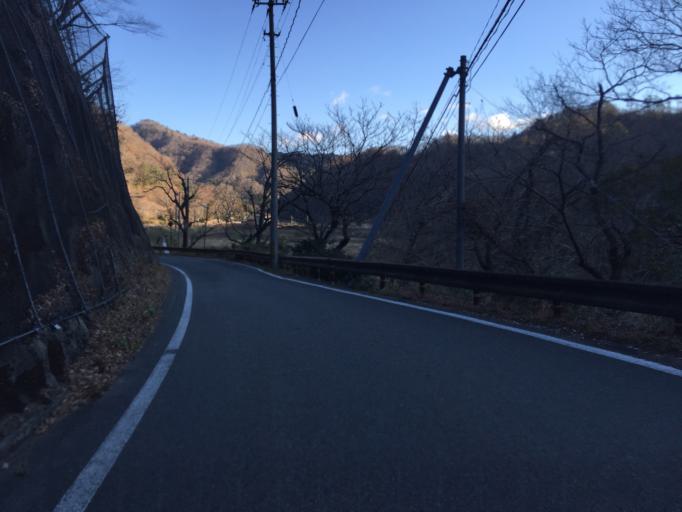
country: JP
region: Fukushima
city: Iwaki
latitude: 37.1826
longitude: 140.8206
